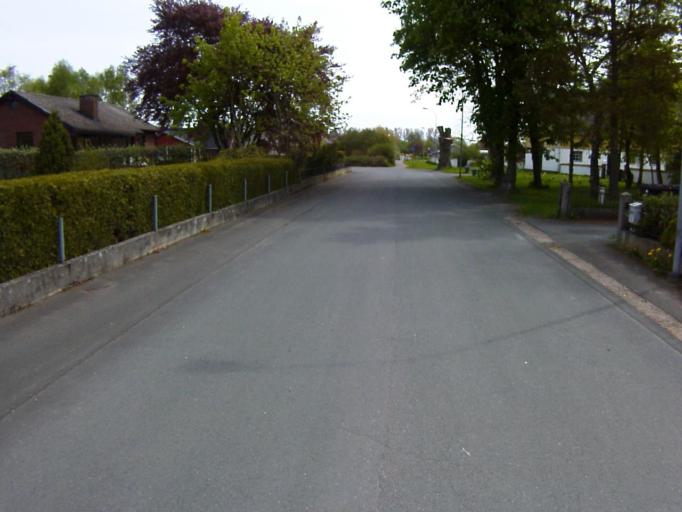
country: SE
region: Skane
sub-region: Kristianstads Kommun
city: Fjalkinge
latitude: 56.0405
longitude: 14.2714
